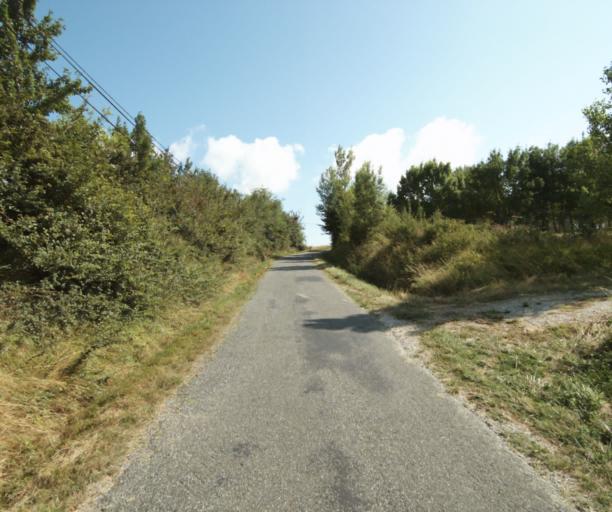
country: FR
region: Midi-Pyrenees
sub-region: Departement de la Haute-Garonne
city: Saint-Felix-Lauragais
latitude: 43.4530
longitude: 1.8328
